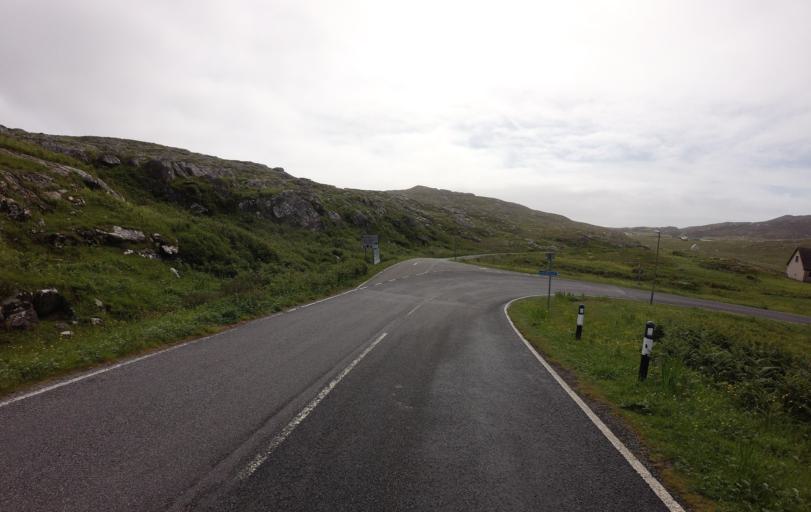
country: GB
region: Scotland
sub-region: Eilean Siar
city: Isle of South Uist
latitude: 57.0740
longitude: -7.3009
